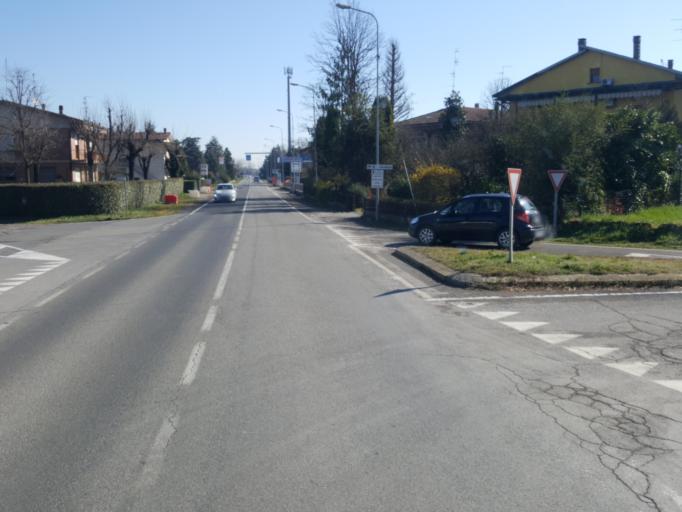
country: IT
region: Emilia-Romagna
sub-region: Provincia di Modena
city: Solara
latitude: 44.7725
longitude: 11.0894
